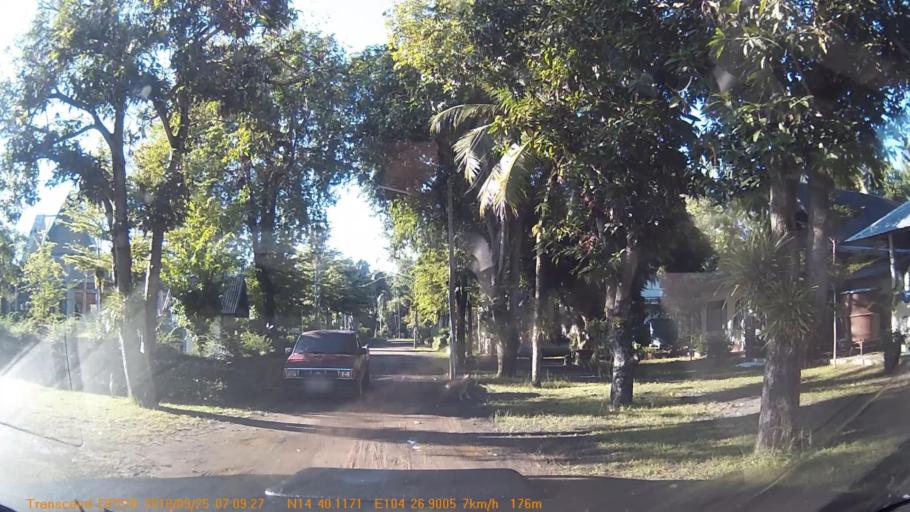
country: TH
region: Sisaket
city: Khun Han
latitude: 14.6684
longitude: 104.4486
